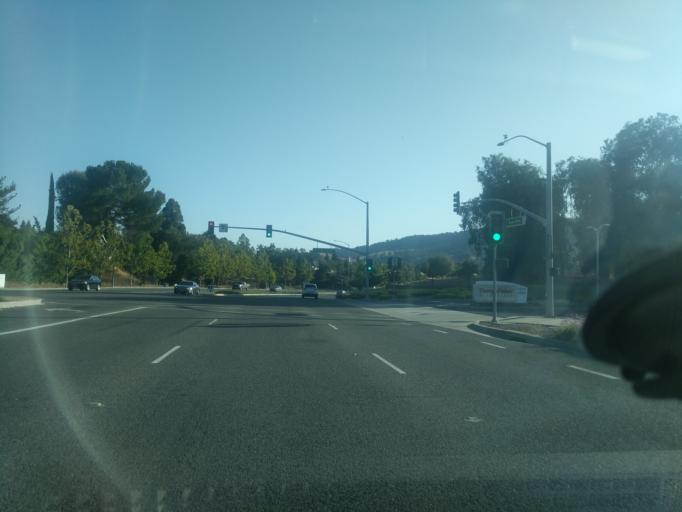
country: US
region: California
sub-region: Alameda County
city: Pleasanton
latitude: 37.6429
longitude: -121.8817
